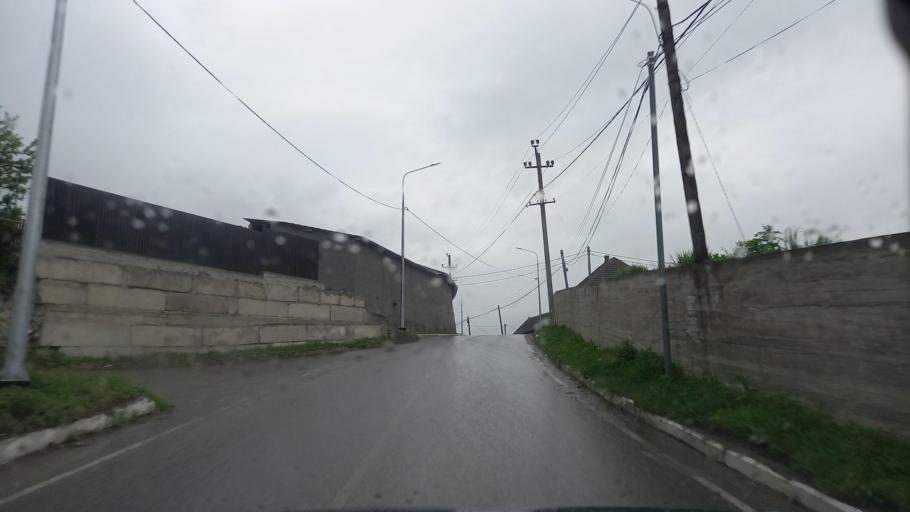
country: RU
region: Kabardino-Balkariya
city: Gundelen
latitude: 43.5997
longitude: 43.1552
